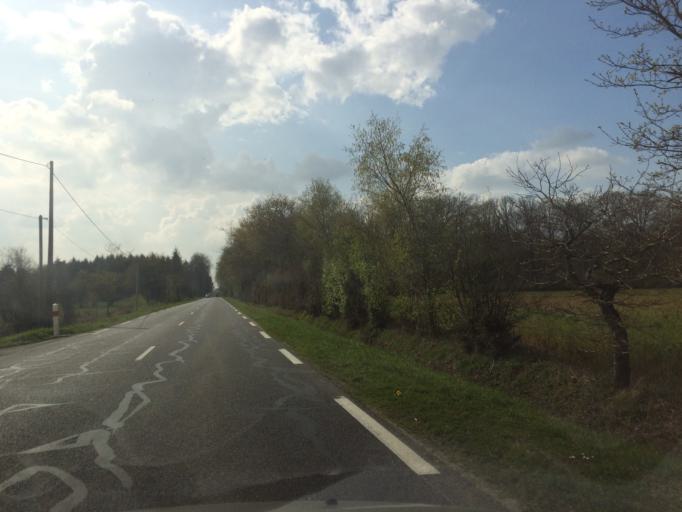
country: FR
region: Pays de la Loire
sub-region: Departement de la Loire-Atlantique
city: Blain
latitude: 47.4852
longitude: -1.8315
